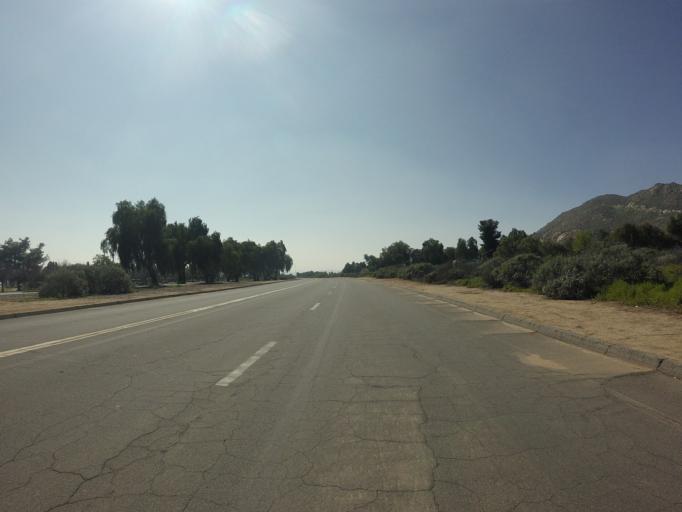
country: US
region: California
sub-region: Riverside County
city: Lakeview
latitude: 33.8728
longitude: -117.1734
